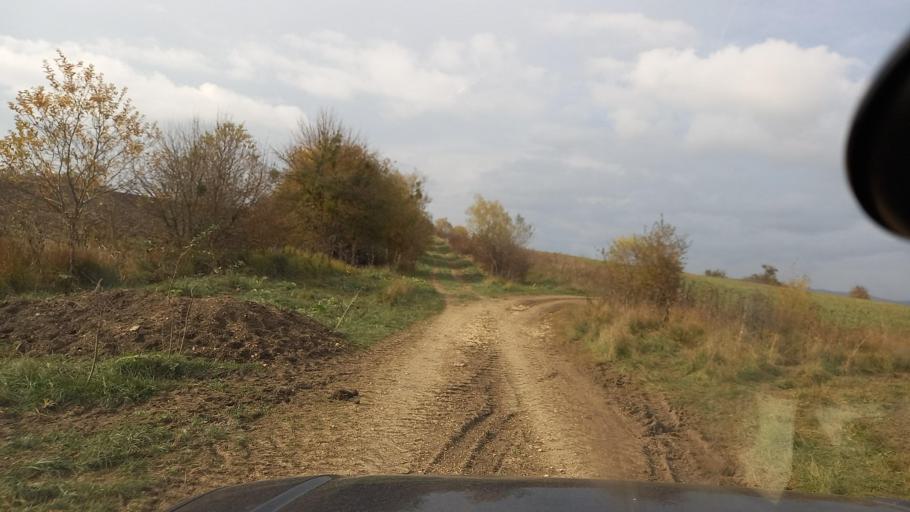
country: RU
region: Krasnodarskiy
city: Gubskaya
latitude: 44.3048
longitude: 40.5516
